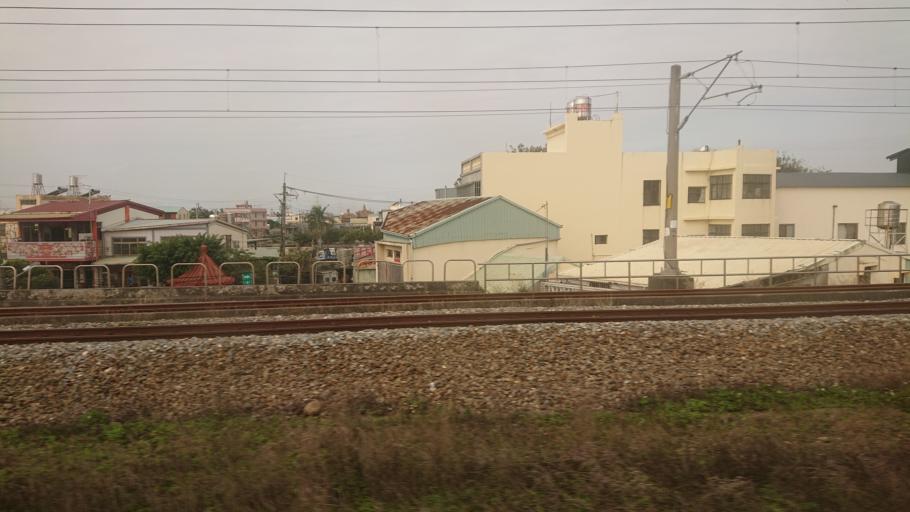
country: TW
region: Taiwan
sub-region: Changhua
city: Chang-hua
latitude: 24.1122
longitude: 120.5789
